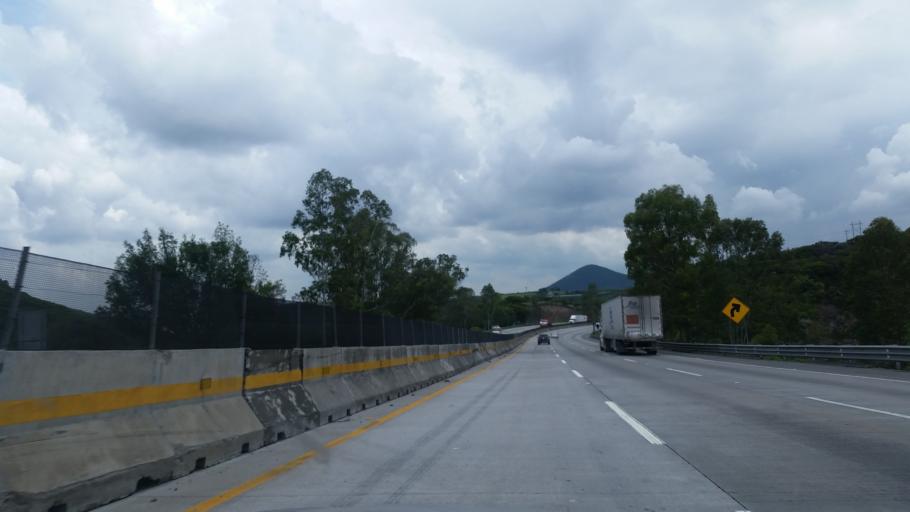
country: MX
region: Hidalgo
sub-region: Tepeji del Rio de Ocampo
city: Santiago Tlautla
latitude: 19.9582
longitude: -99.4171
